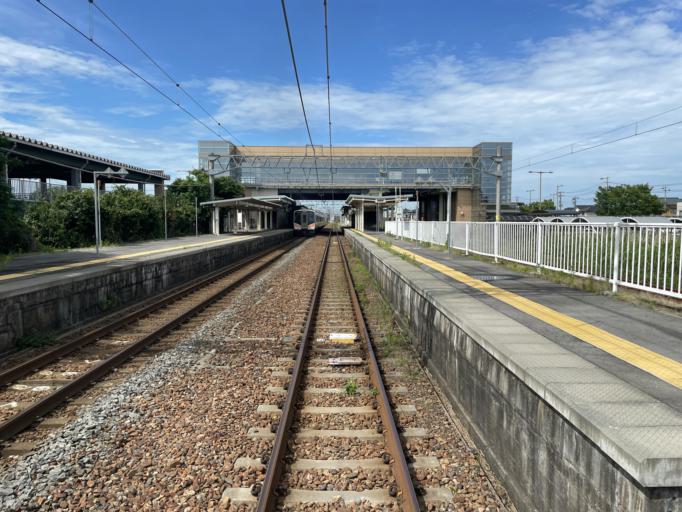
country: JP
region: Niigata
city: Suibara
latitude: 37.9200
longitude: 139.2159
